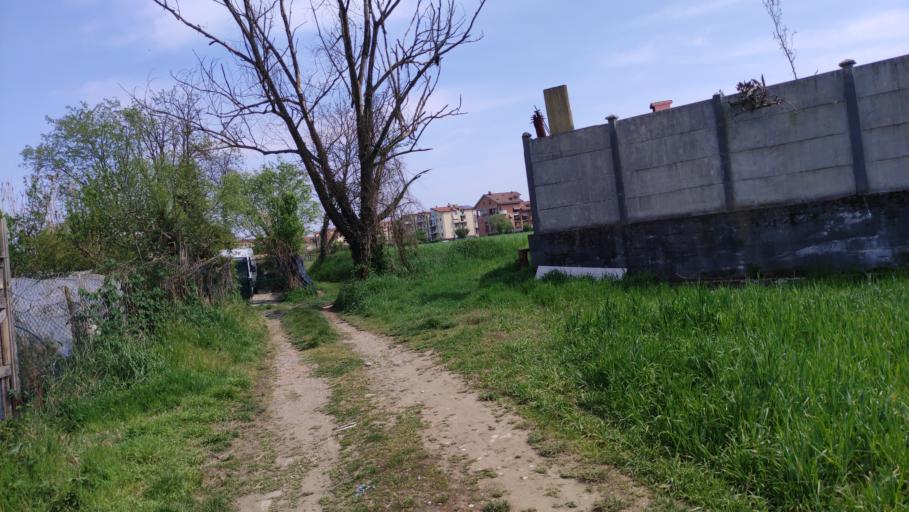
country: IT
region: Piedmont
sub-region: Provincia di Torino
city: Nichelino
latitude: 45.0060
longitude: 7.6402
